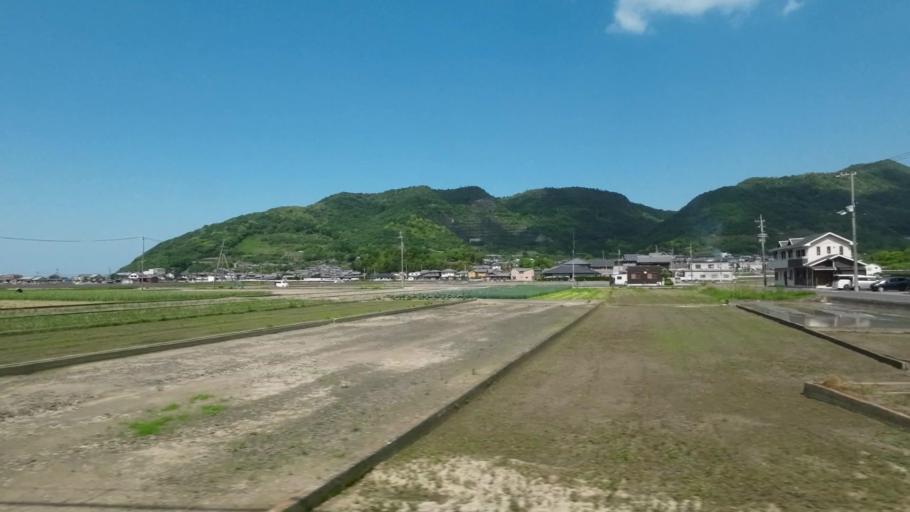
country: JP
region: Kagawa
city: Kan'onjicho
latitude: 34.1446
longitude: 133.6860
